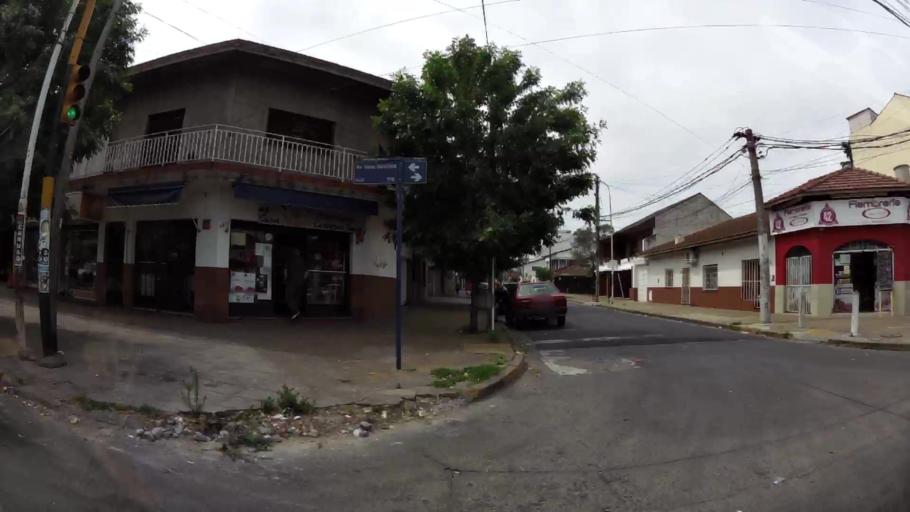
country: AR
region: Buenos Aires F.D.
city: Villa Lugano
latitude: -34.6960
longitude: -58.5045
